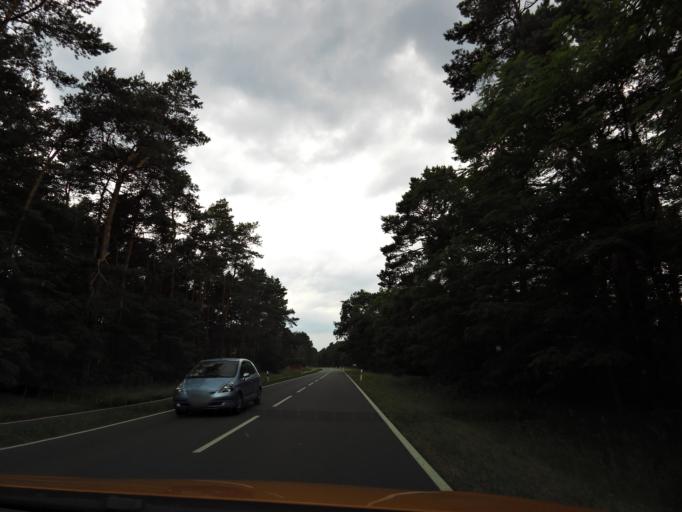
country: DE
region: Brandenburg
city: Baruth
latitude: 52.0370
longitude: 13.5198
